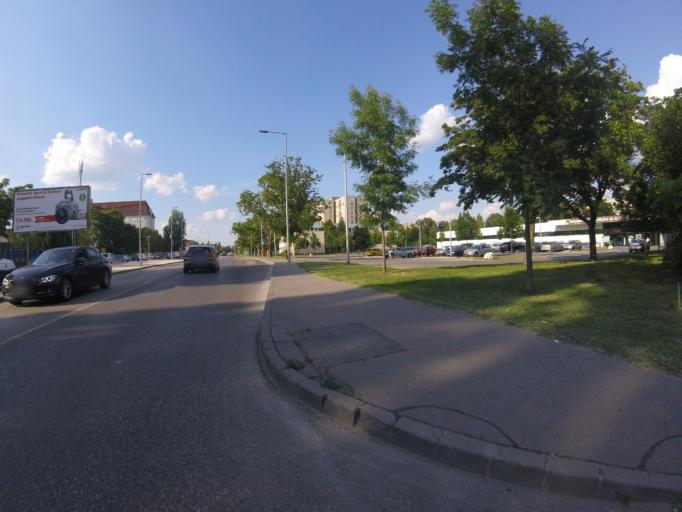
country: HU
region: Budapest
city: Budapest III. keruelet
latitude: 47.5542
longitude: 19.0405
